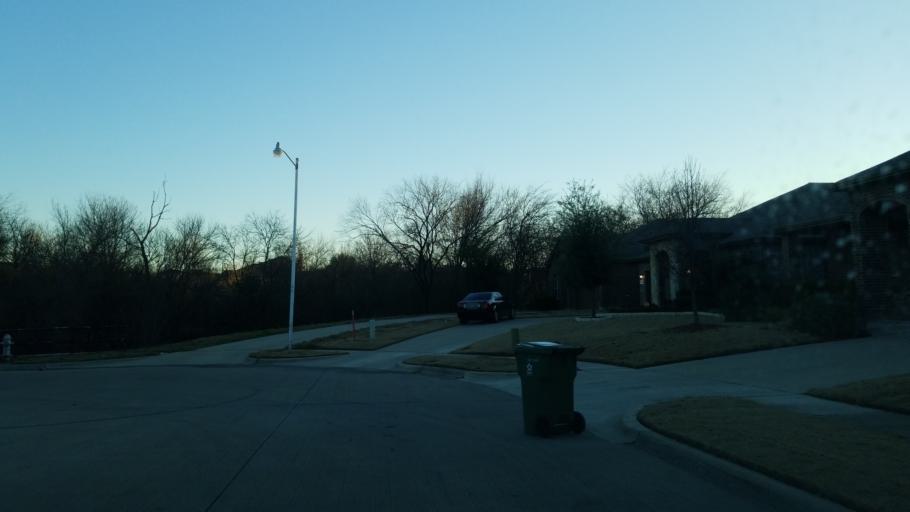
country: US
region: Texas
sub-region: Tarrant County
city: Arlington
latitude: 32.7254
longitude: -97.0563
